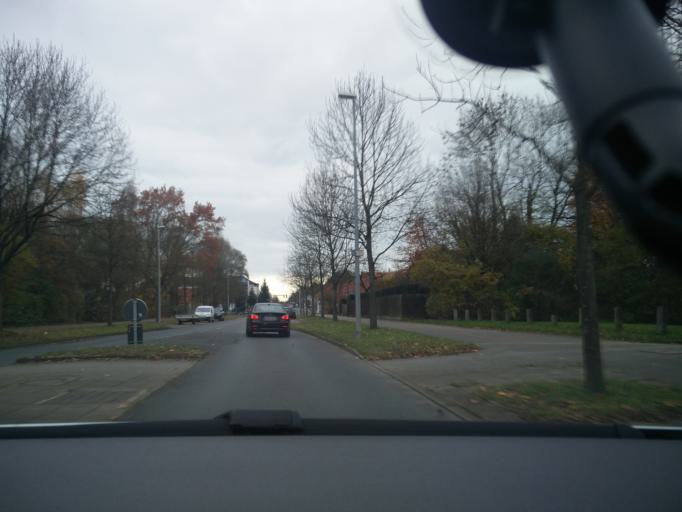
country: DE
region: Lower Saxony
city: Laatzen
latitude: 52.3439
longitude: 9.8213
